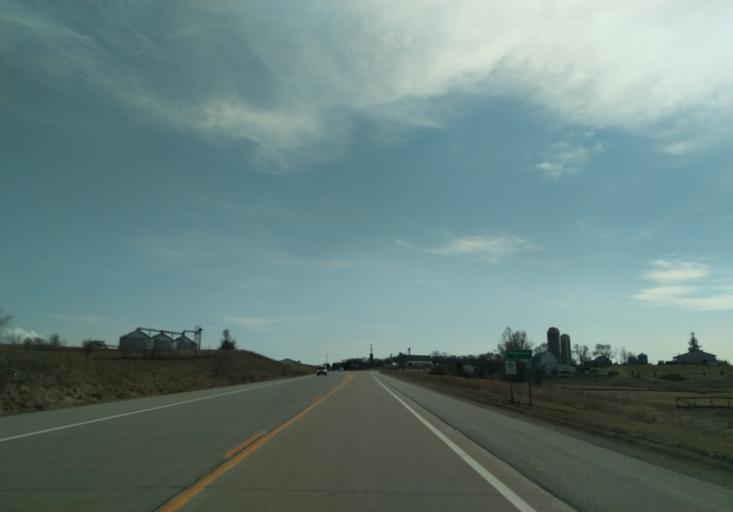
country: US
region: Minnesota
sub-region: Fillmore County
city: Preston
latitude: 43.6922
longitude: -92.0987
